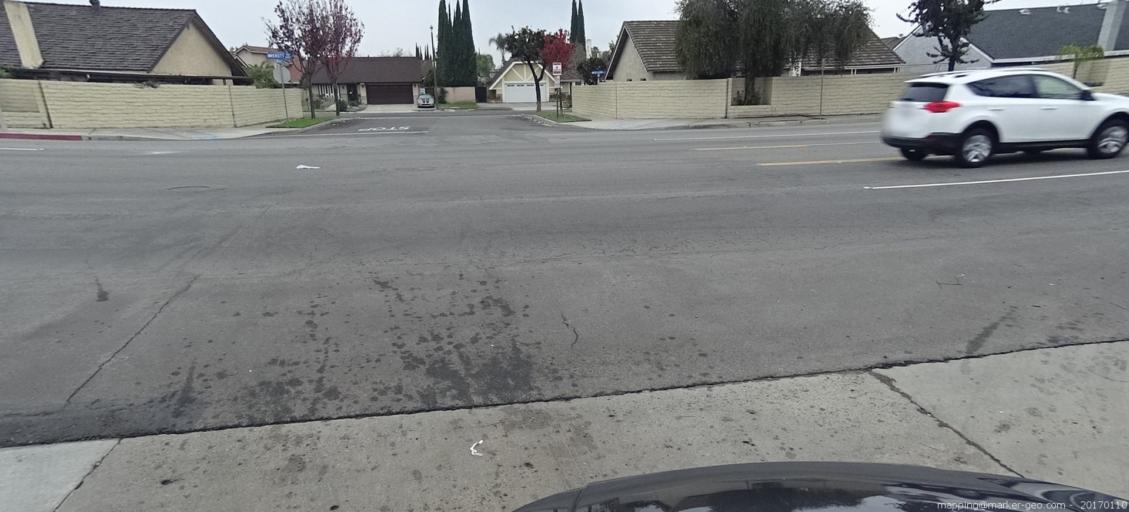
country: US
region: California
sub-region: Orange County
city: Stanton
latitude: 33.8055
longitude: -118.0105
